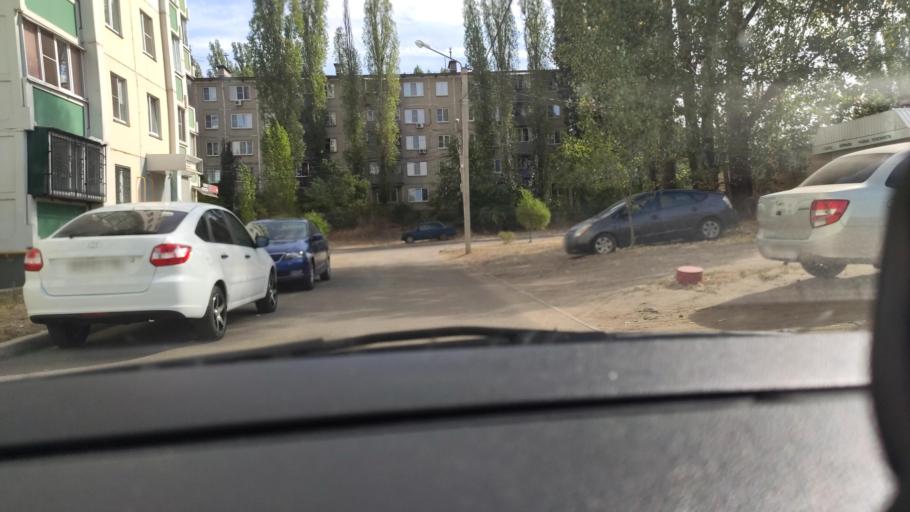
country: RU
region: Voronezj
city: Pridonskoy
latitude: 51.6258
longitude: 39.0679
